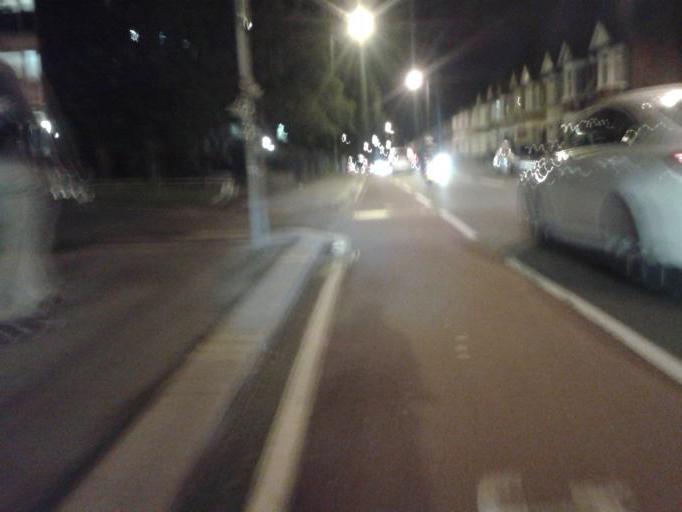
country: GB
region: England
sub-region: Greater London
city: Walthamstow
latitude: 51.5875
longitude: -0.0371
